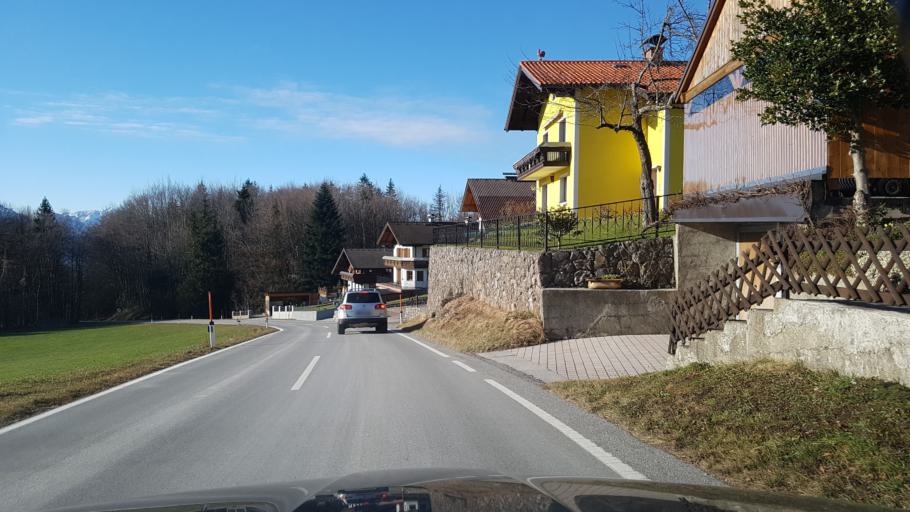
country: AT
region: Salzburg
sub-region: Politischer Bezirk Salzburg-Umgebung
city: Elsbethen
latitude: 47.7713
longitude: 13.1027
